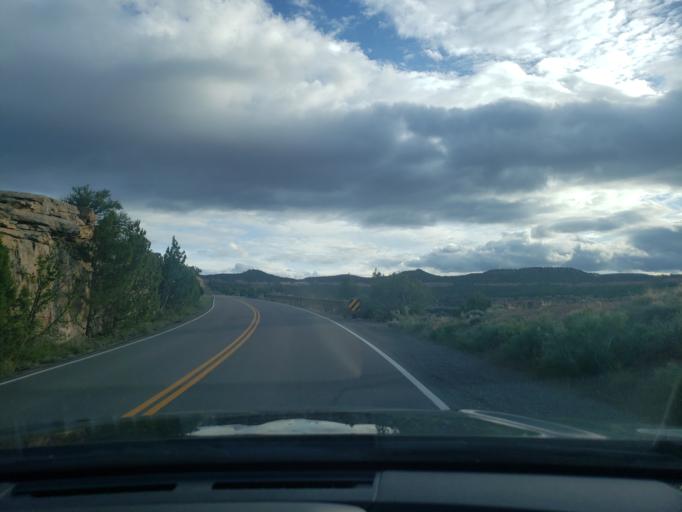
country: US
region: Colorado
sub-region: Mesa County
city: Redlands
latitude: 39.0306
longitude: -108.6544
